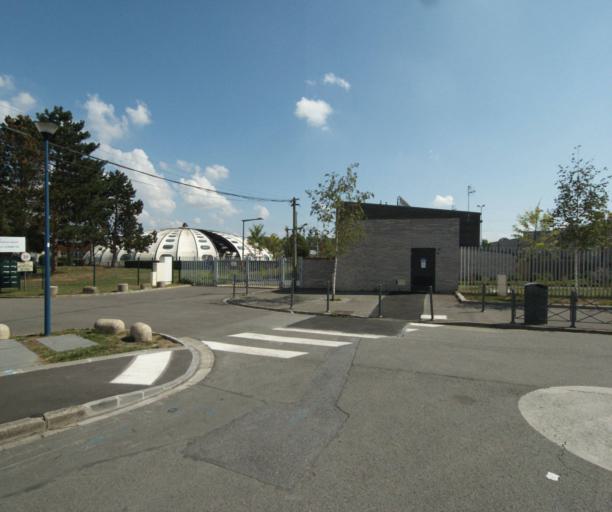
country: FR
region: Nord-Pas-de-Calais
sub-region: Departement du Nord
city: Mons-en-Baroeul
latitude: 50.6295
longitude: 3.1178
